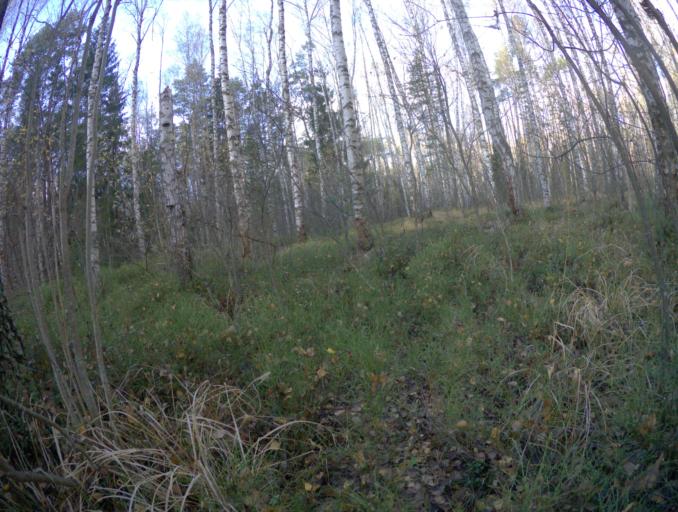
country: RU
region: Vladimir
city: Raduzhnyy
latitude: 56.0583
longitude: 40.3423
